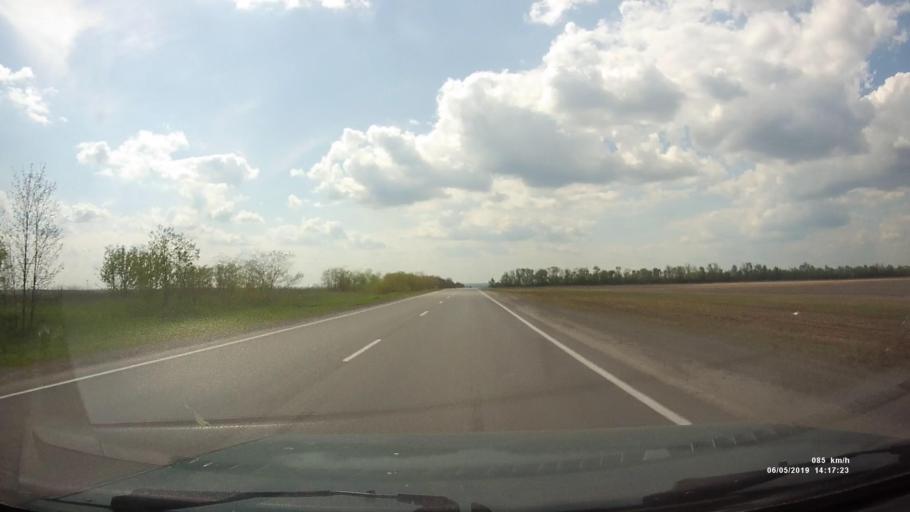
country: RU
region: Rostov
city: Kamenolomni
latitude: 47.6336
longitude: 40.2704
